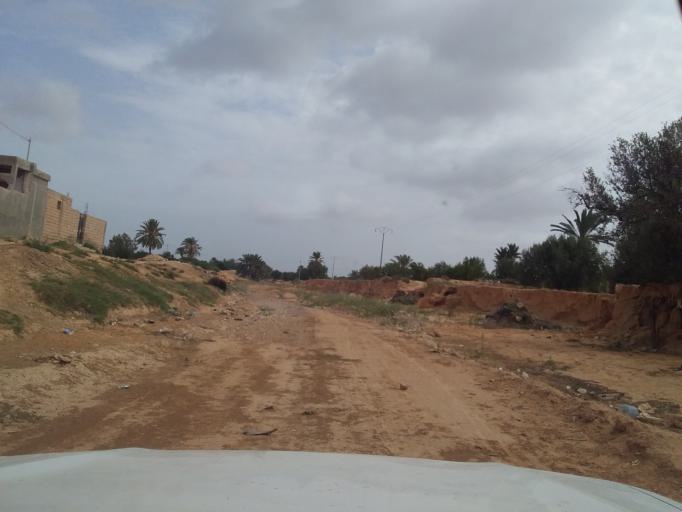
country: TN
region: Qabis
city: Gabes
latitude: 33.6277
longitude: 10.2964
